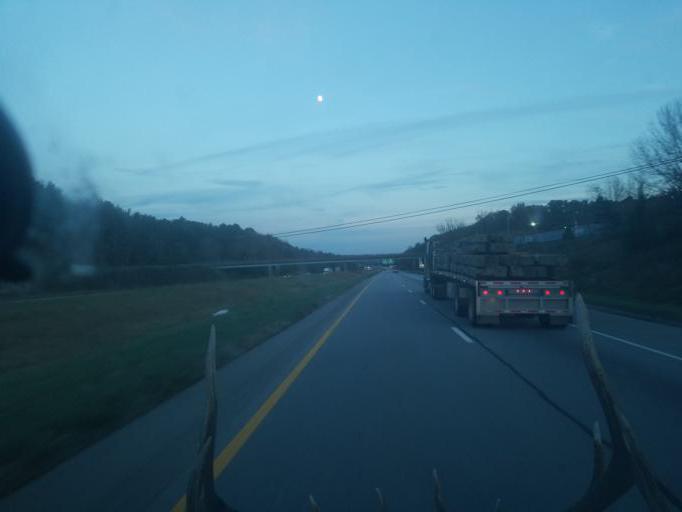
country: US
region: Ohio
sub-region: Guernsey County
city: Cambridge
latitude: 40.0079
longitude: -81.6036
